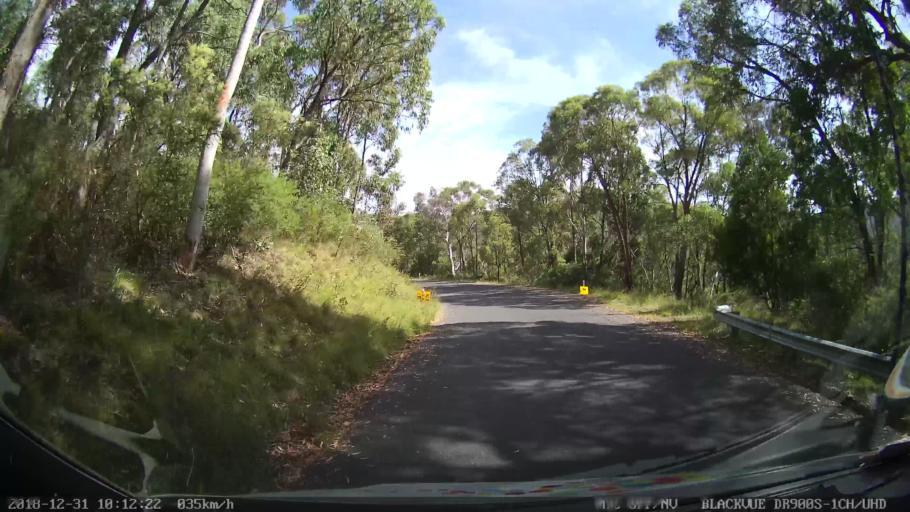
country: AU
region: New South Wales
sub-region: Snowy River
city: Jindabyne
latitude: -36.5371
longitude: 148.1619
